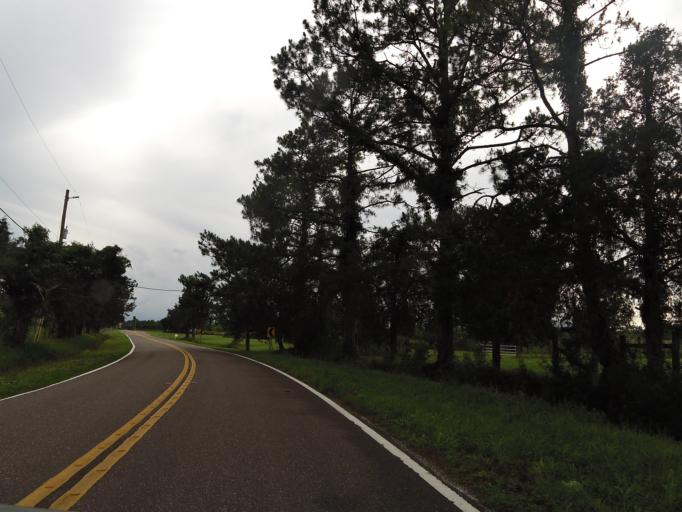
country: US
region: Florida
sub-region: Nassau County
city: Nassau Village-Ratliff
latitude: 30.5466
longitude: -81.7157
